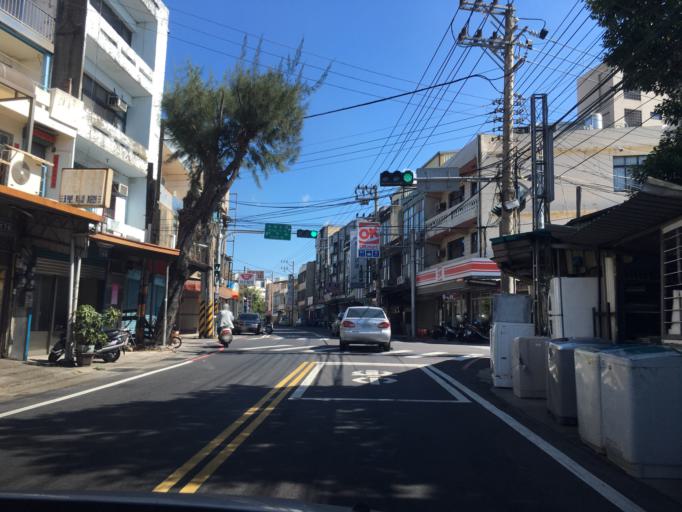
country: TW
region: Taiwan
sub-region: Hsinchu
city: Hsinchu
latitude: 24.8055
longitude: 120.9378
